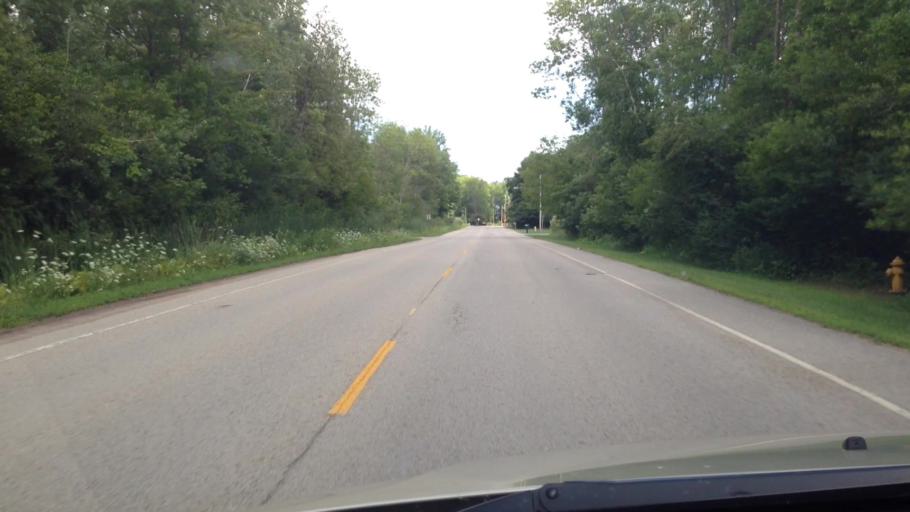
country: US
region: Michigan
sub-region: Menominee County
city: Menominee
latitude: 45.1440
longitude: -87.6082
